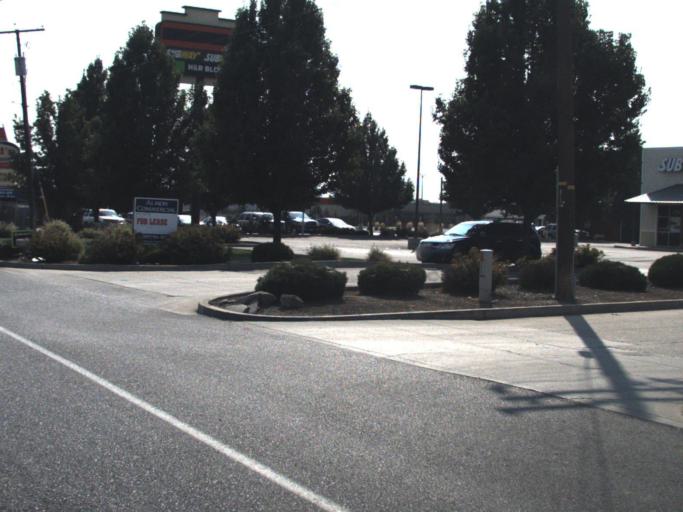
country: US
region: Washington
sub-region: Yakima County
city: Toppenish
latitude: 46.3742
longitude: -120.3202
